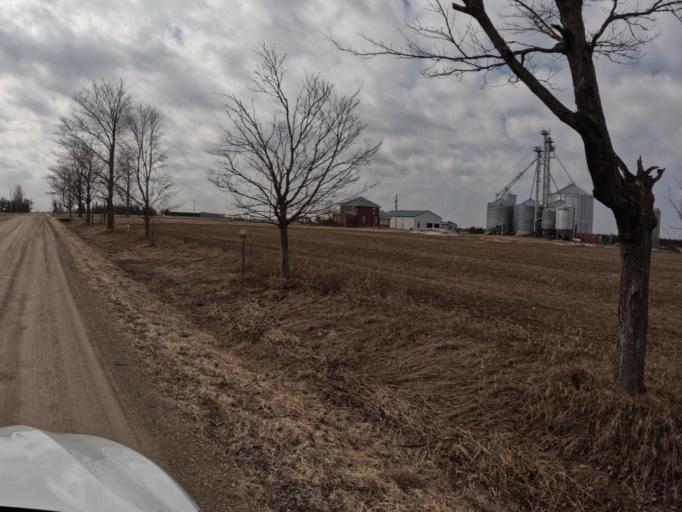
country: CA
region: Ontario
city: Orangeville
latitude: 43.9206
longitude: -80.2395
